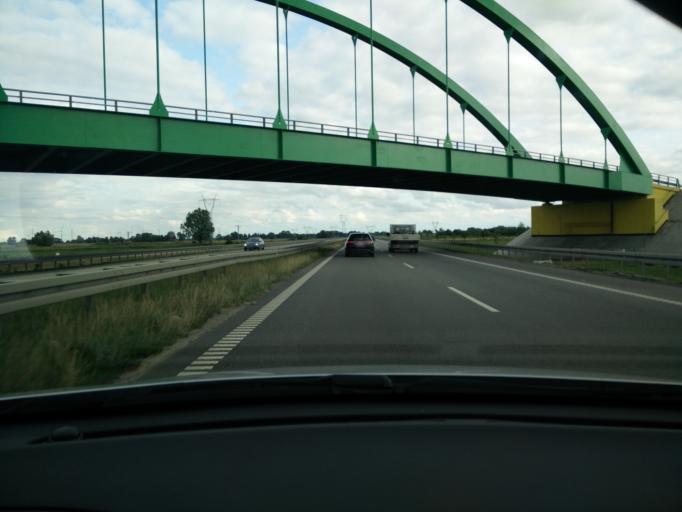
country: PL
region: Pomeranian Voivodeship
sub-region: Gdansk
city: Gdansk
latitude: 54.3329
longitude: 18.7036
